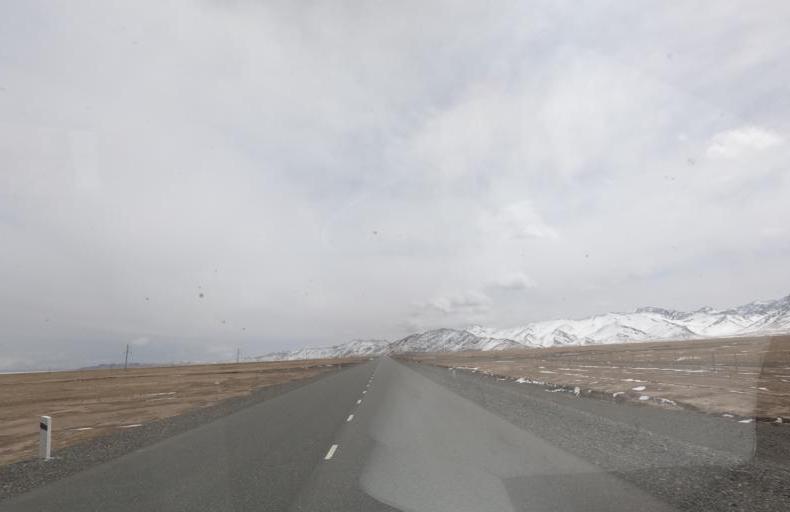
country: KG
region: Naryn
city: Baetov
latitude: 40.5526
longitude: 75.2154
